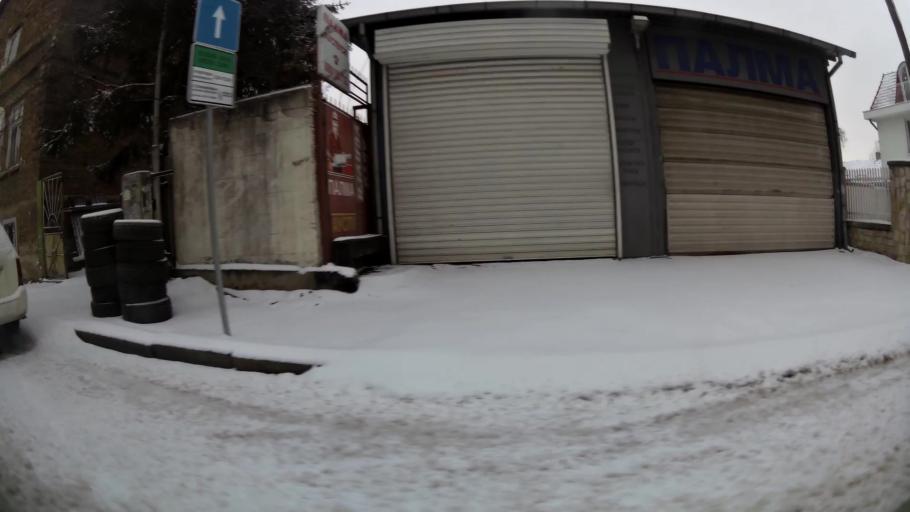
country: BG
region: Sofia-Capital
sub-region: Stolichna Obshtina
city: Sofia
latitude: 42.7057
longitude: 23.3067
